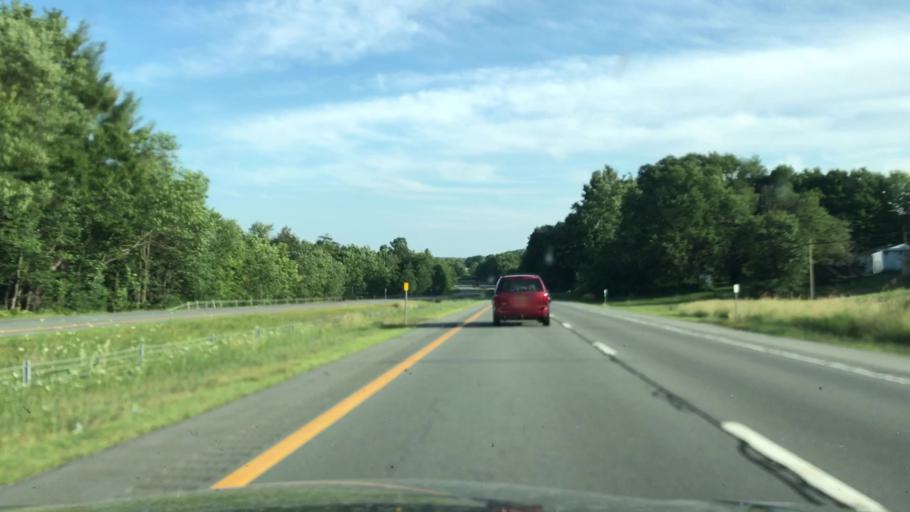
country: US
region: New York
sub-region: Sullivan County
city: Liberty
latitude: 41.7488
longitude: -74.7336
